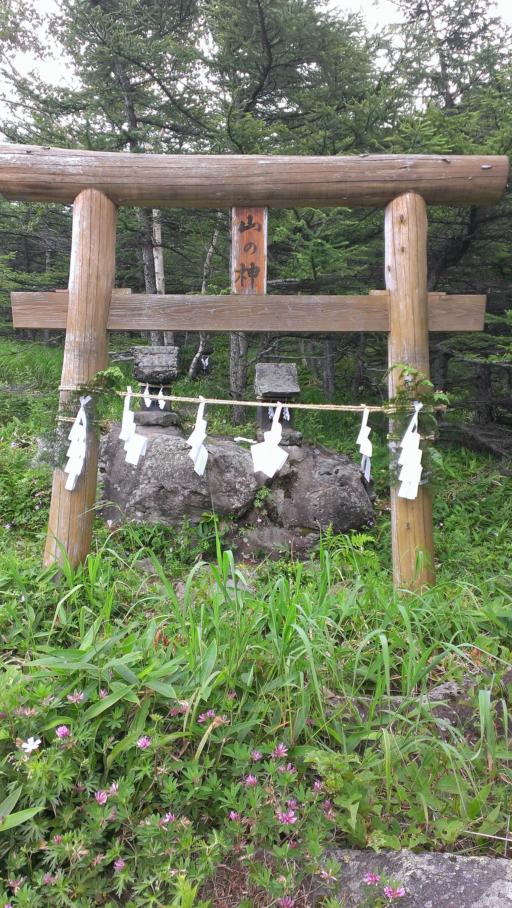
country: JP
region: Nagano
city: Komoro
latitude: 36.4043
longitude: 138.4697
